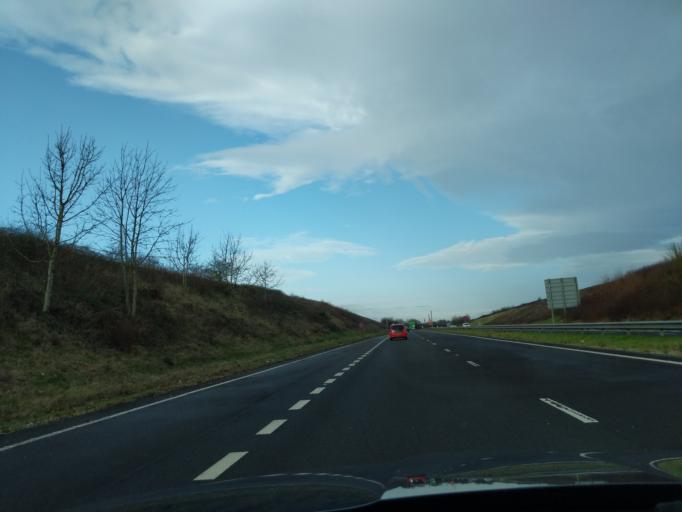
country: GB
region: England
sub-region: Northumberland
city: Ponteland
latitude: 55.0308
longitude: -1.7107
